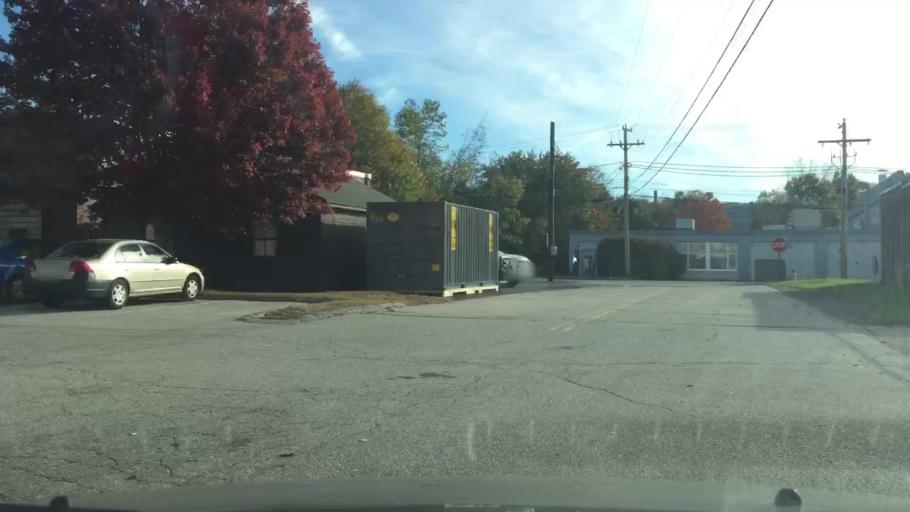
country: US
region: New Hampshire
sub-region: Cheshire County
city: Keene
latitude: 42.9325
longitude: -72.2947
